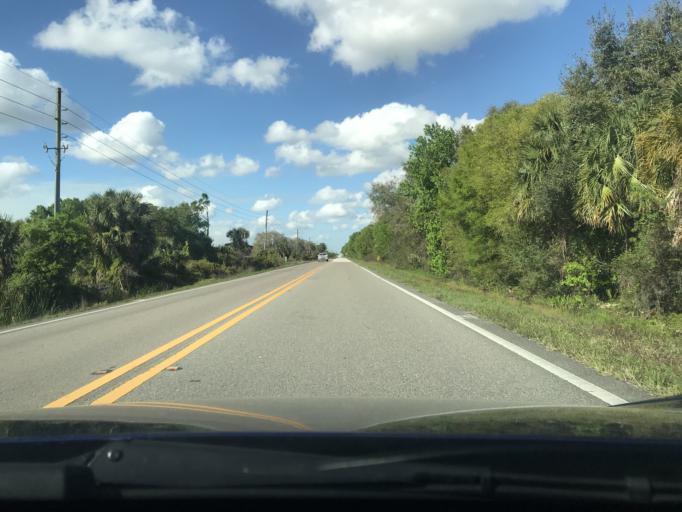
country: US
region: Florida
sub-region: Okeechobee County
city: Taylor Creek
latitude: 27.2216
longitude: -80.6942
